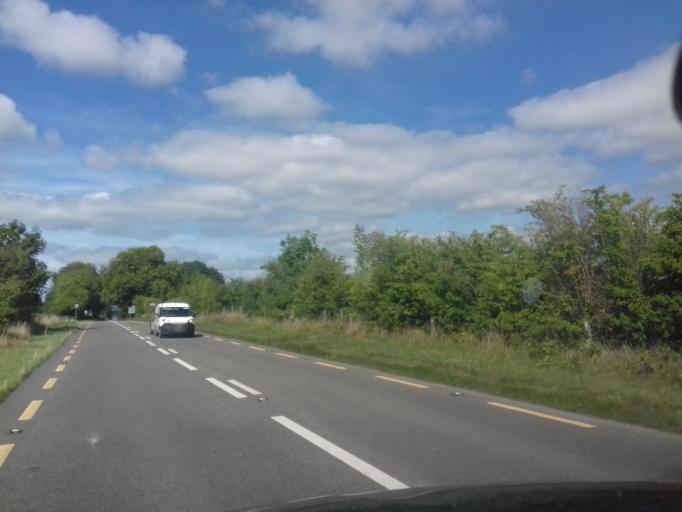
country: IE
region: Leinster
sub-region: Wicklow
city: Blessington
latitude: 53.1479
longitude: -6.5570
